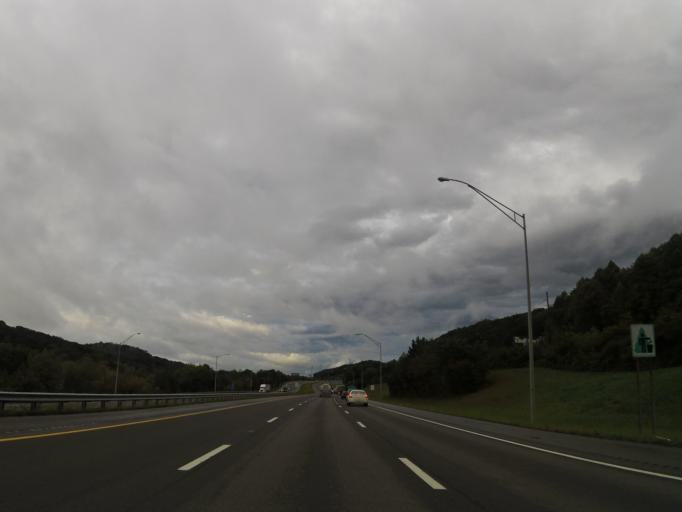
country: US
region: Tennessee
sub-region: Knox County
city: Knoxville
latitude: 36.0289
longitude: -83.8981
